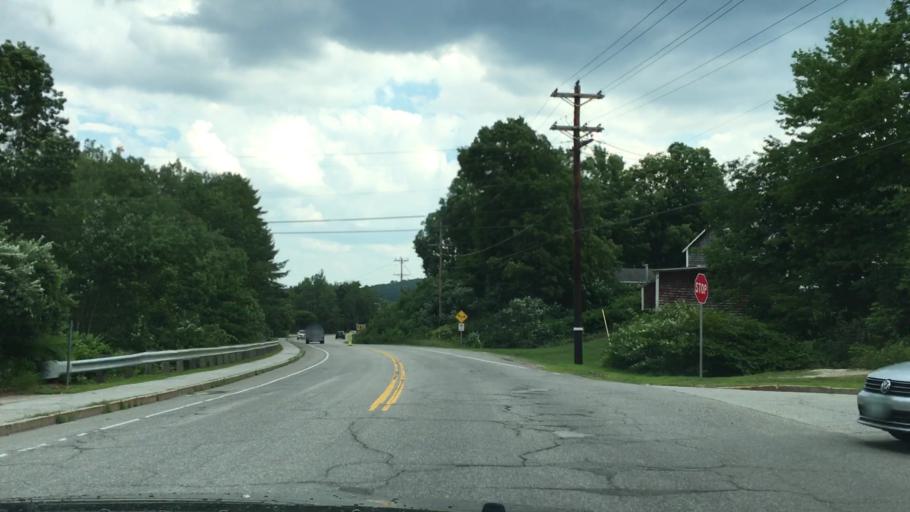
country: US
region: New Hampshire
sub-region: Belknap County
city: Meredith
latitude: 43.6662
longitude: -71.5025
